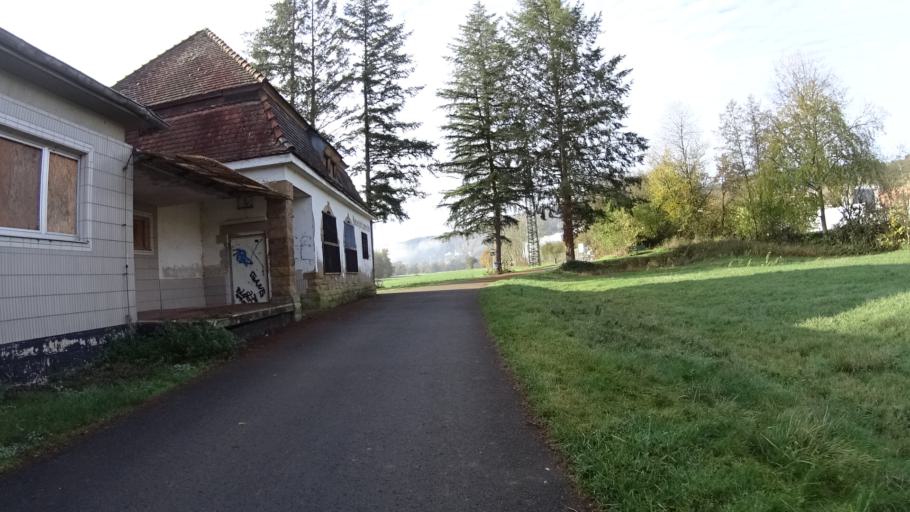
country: DE
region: Rheinland-Pfalz
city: Lauterecken
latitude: 49.6474
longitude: 7.5851
